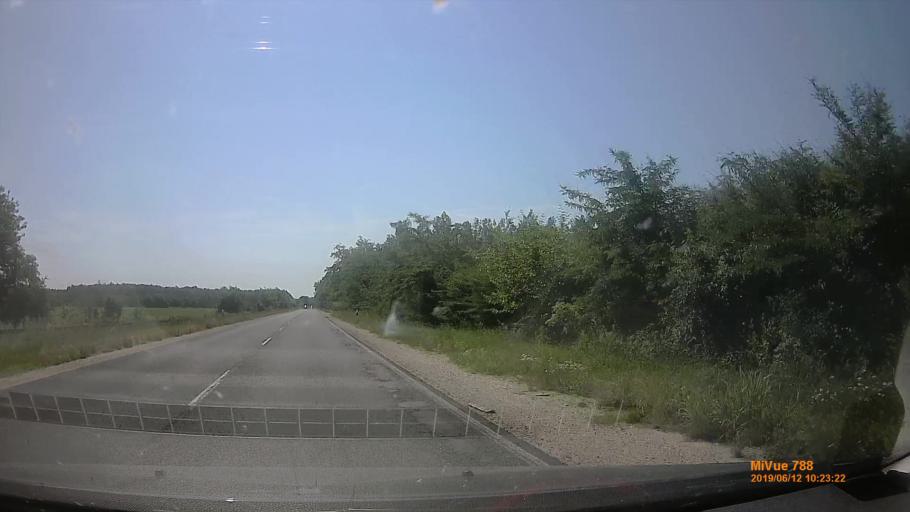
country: HU
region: Pest
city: Ujhartyan
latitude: 47.1700
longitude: 19.3694
